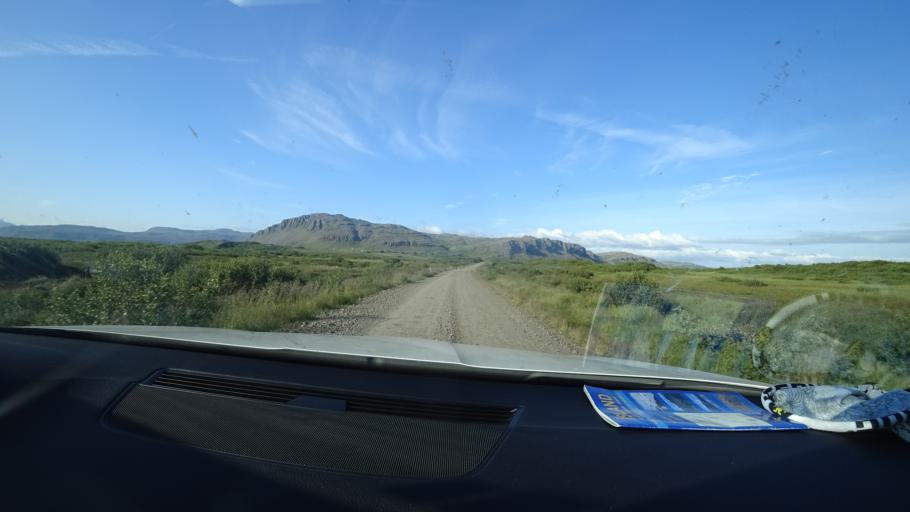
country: IS
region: West
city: Borgarnes
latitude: 64.6804
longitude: -21.9532
